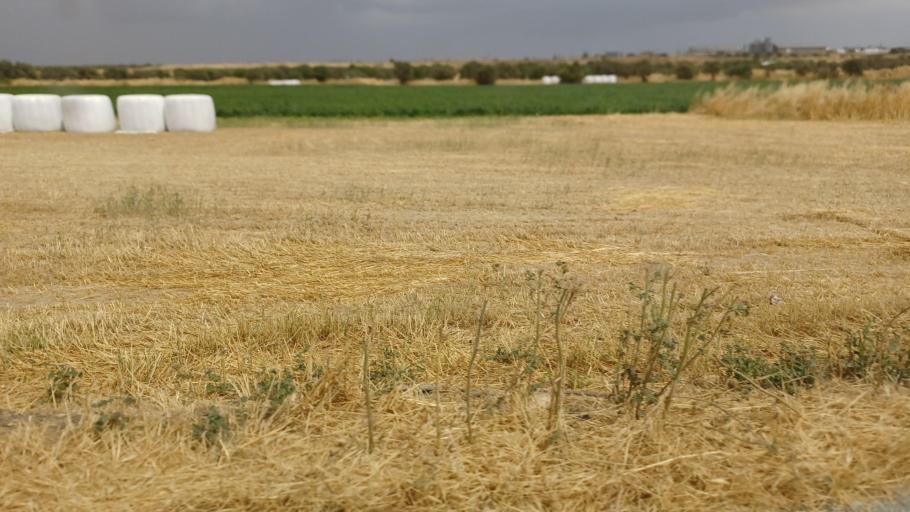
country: CY
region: Larnaka
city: Athienou
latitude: 35.0701
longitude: 33.5222
